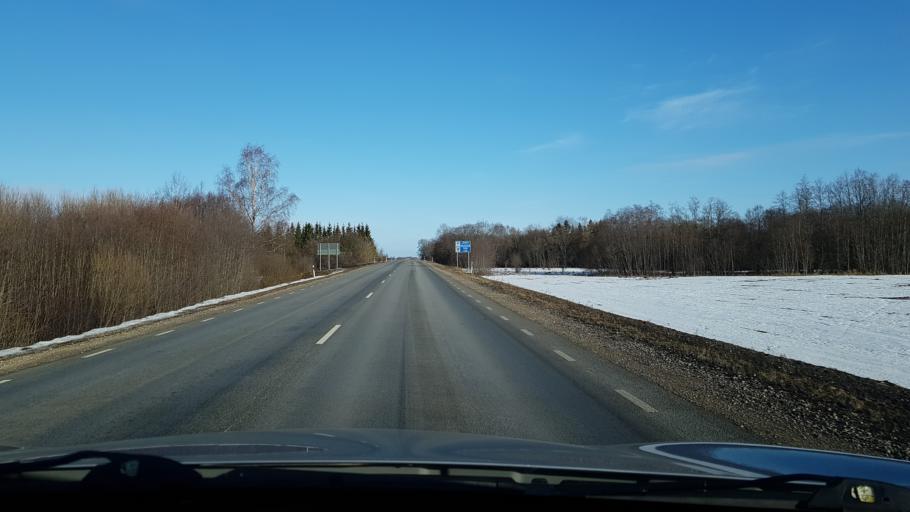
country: EE
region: Viljandimaa
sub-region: Vohma linn
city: Vohma
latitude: 58.6352
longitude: 25.5737
